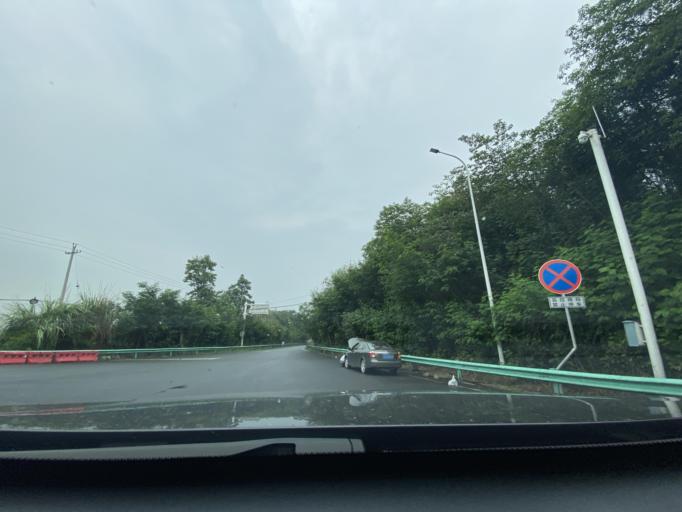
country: CN
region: Sichuan
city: Wenlin
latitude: 30.2949
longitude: 104.1203
